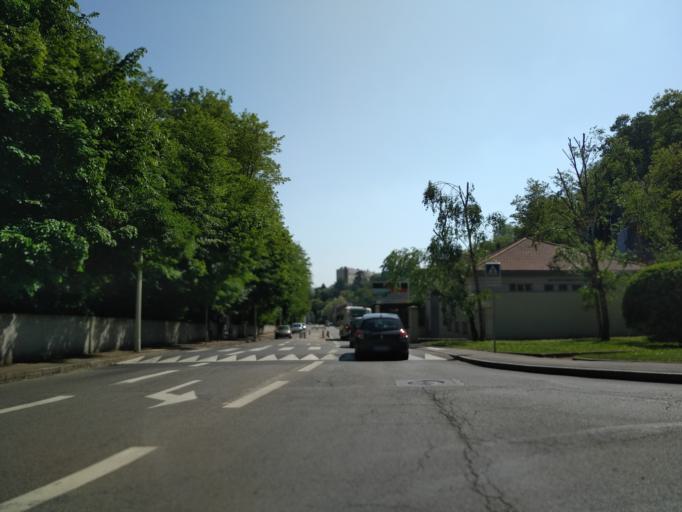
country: FR
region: Rhone-Alpes
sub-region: Departement du Rhone
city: Caluire-et-Cuire
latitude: 45.7918
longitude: 4.8088
